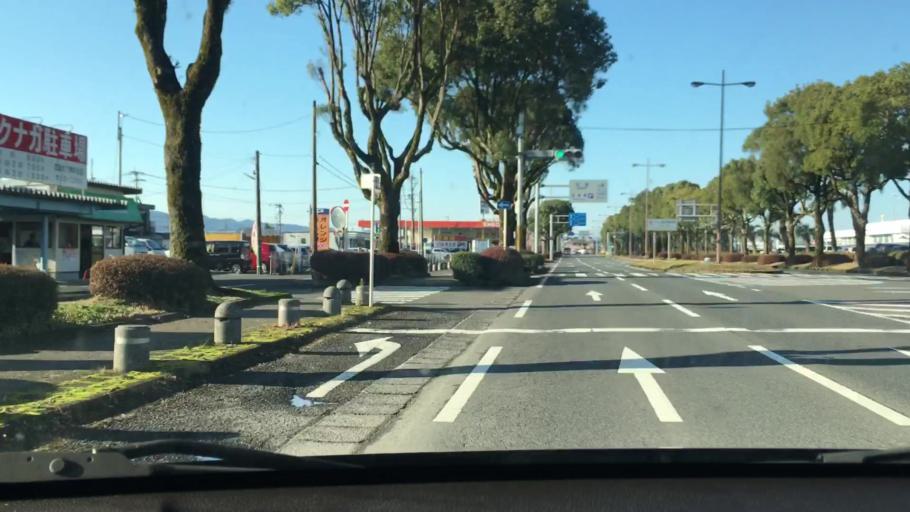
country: JP
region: Kagoshima
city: Kajiki
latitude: 31.7990
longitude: 130.7157
